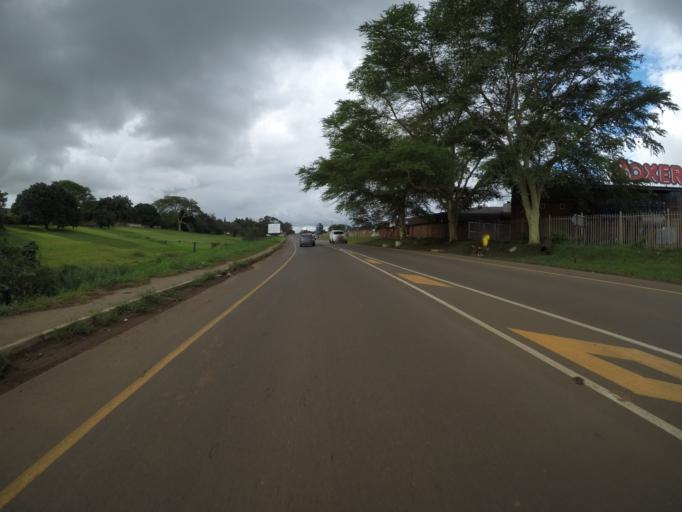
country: ZA
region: KwaZulu-Natal
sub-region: uMkhanyakude District Municipality
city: Mtubatuba
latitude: -28.4165
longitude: 32.1840
